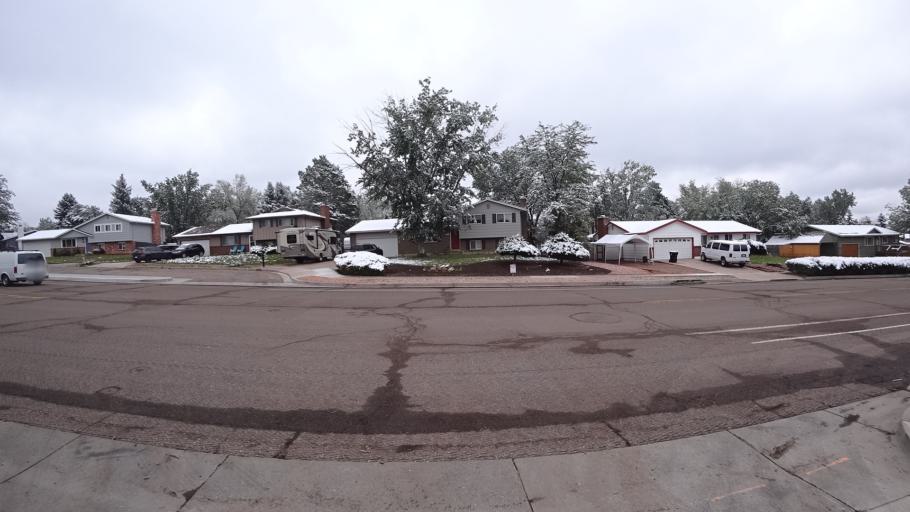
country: US
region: Colorado
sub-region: El Paso County
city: Colorado Springs
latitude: 38.8978
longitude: -104.7721
